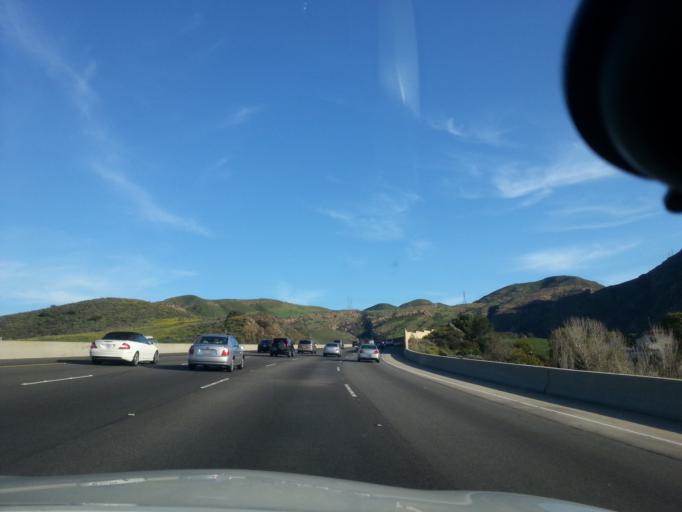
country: US
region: California
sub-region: Ventura County
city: Casa Conejo
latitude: 34.2044
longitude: -118.9819
